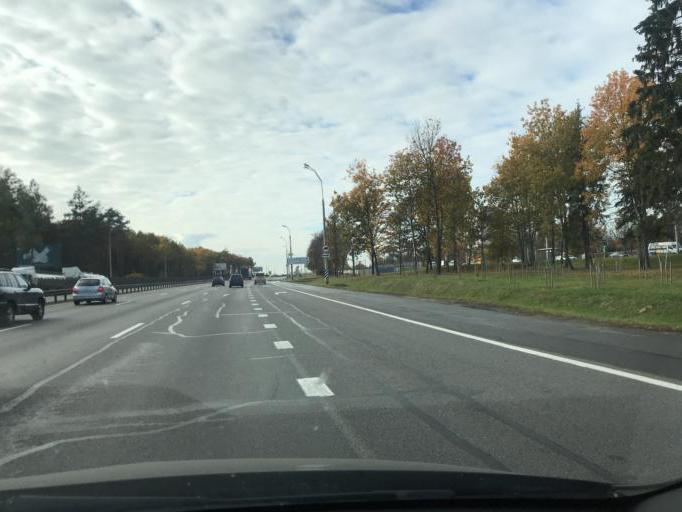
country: BY
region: Minsk
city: Hatava
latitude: 53.8344
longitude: 27.6466
